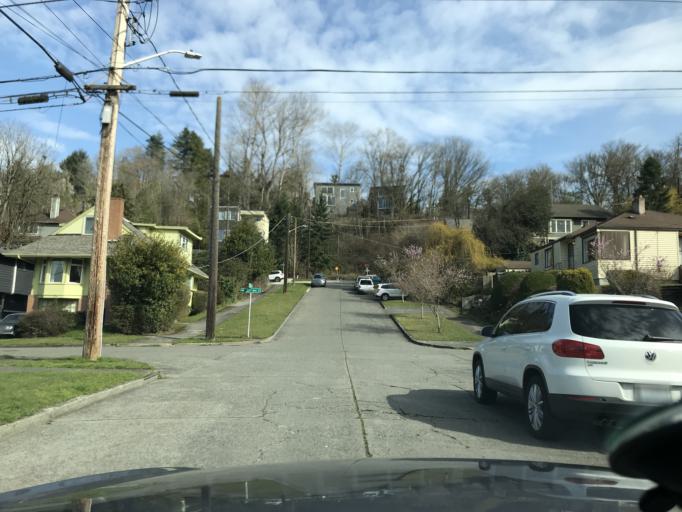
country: US
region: Washington
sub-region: King County
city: Seattle
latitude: 47.6189
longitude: -122.2926
